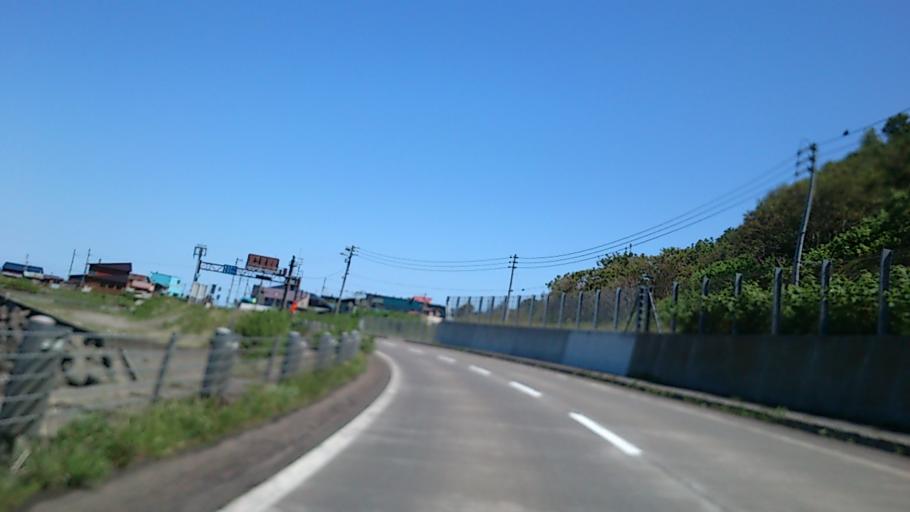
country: JP
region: Hokkaido
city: Rumoi
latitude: 43.7346
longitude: 141.3385
